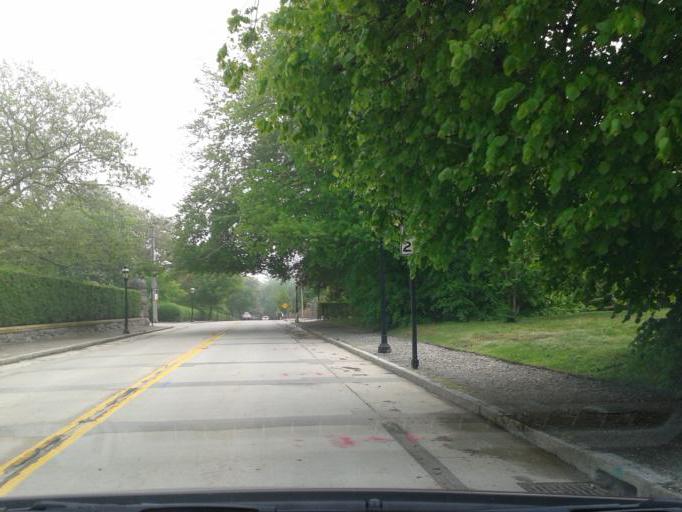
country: US
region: Rhode Island
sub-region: Newport County
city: Newport
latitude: 41.4558
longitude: -71.3095
